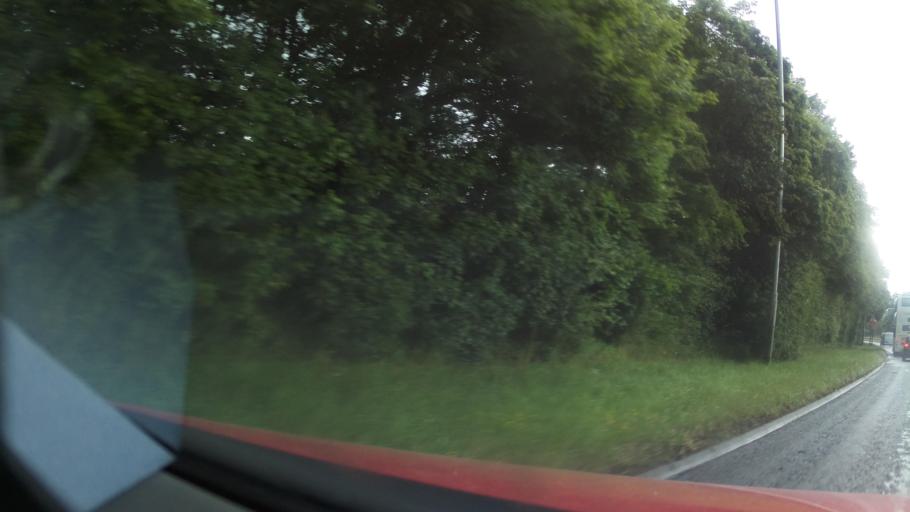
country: GB
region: England
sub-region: Dudley
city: Kingswinford
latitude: 52.5449
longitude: -2.1735
